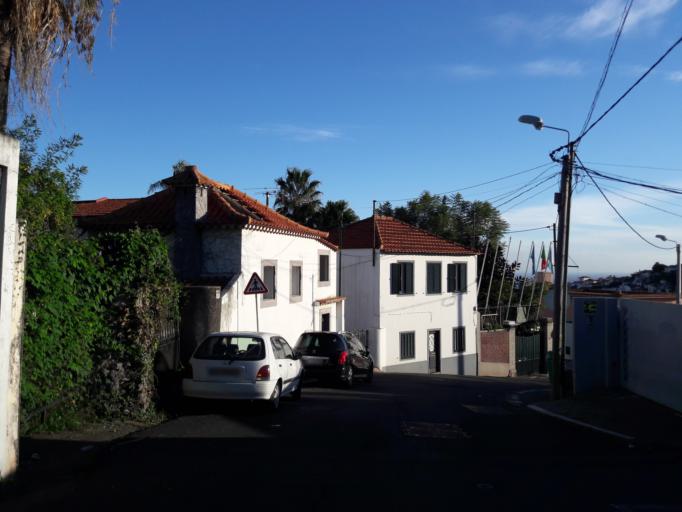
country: PT
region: Madeira
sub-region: Funchal
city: Nossa Senhora do Monte
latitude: 32.6578
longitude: -16.9153
